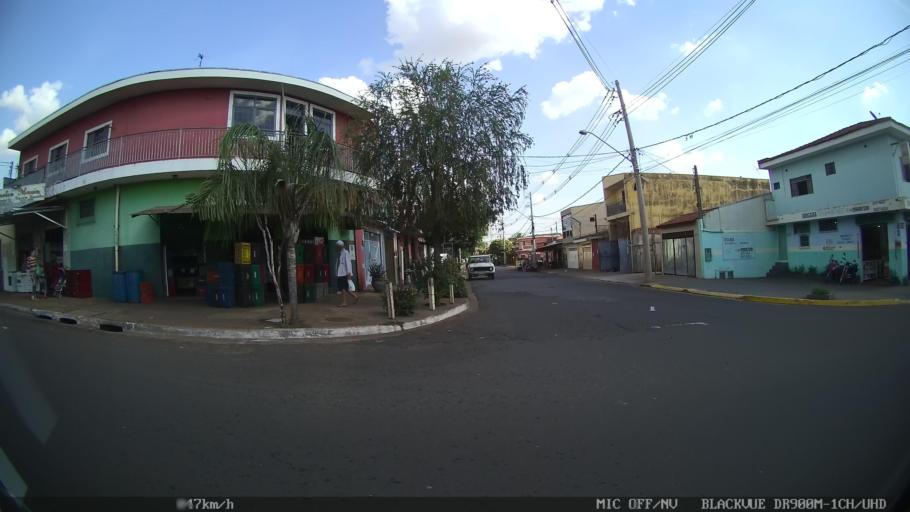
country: BR
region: Sao Paulo
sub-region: Ribeirao Preto
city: Ribeirao Preto
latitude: -21.2002
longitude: -47.8458
